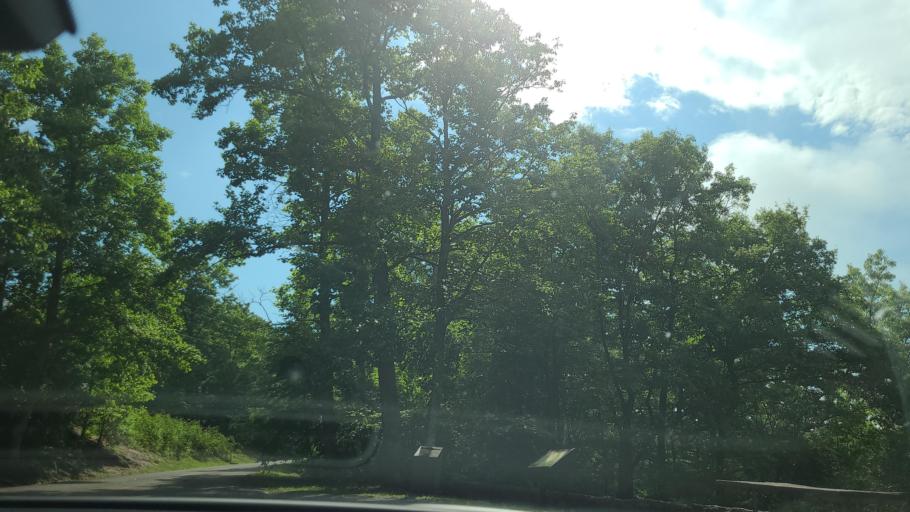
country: US
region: Kentucky
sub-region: Bell County
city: Pineville
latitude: 36.7535
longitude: -83.7088
